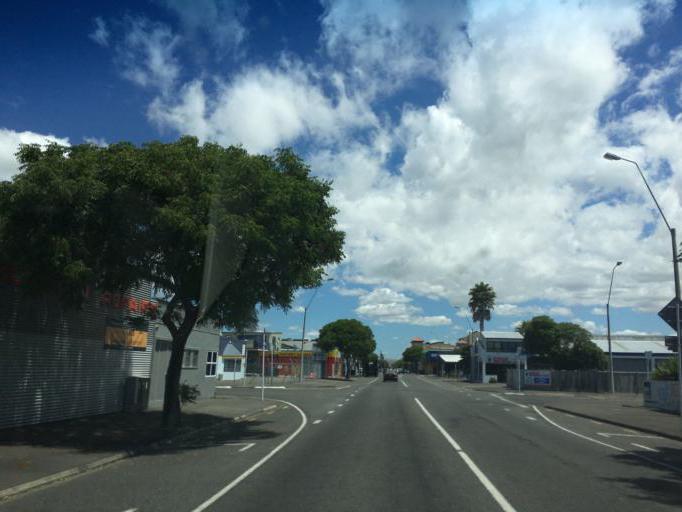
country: NZ
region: Hawke's Bay
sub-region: Hastings District
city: Hastings
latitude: -39.6431
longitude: 176.8488
